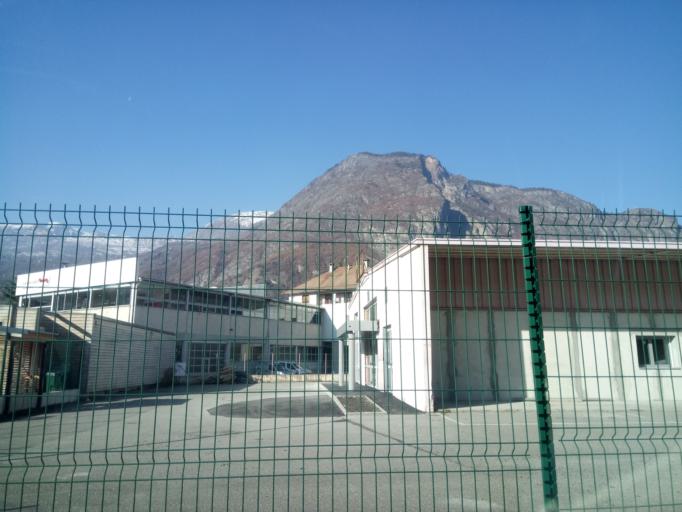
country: FR
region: Rhone-Alpes
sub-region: Departement de la Savoie
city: Saint-Jean-de-Maurienne
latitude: 45.2755
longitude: 6.3570
